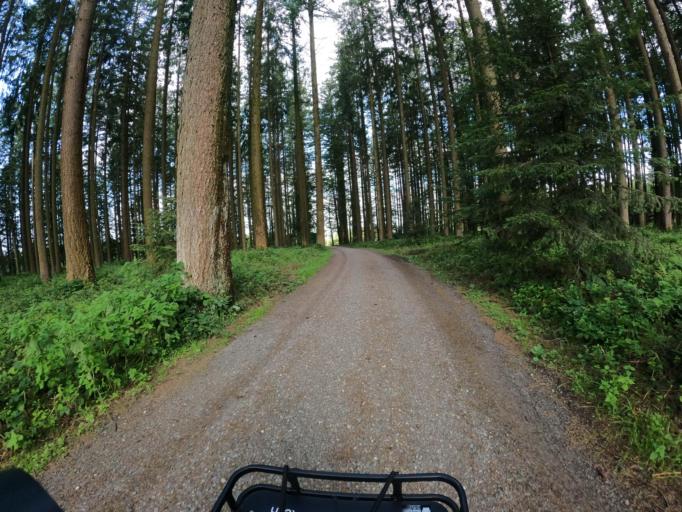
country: CH
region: Aargau
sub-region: Bezirk Muri
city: Buttwil
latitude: 47.2271
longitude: 8.3134
